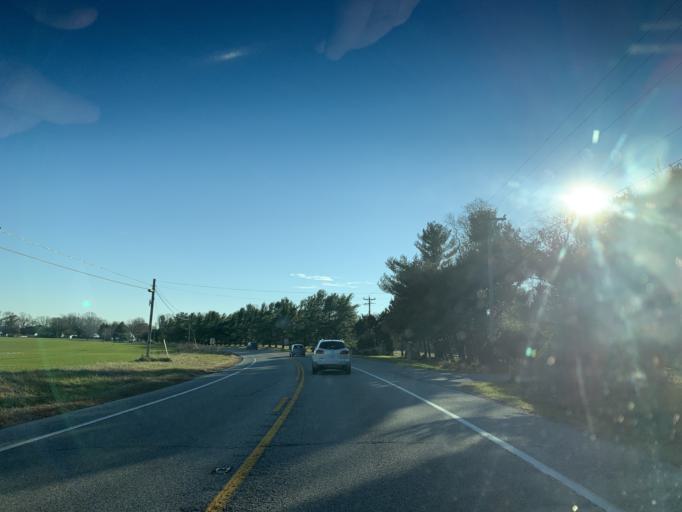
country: US
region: Delaware
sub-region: New Castle County
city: Middletown
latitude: 39.3735
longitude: -75.8832
